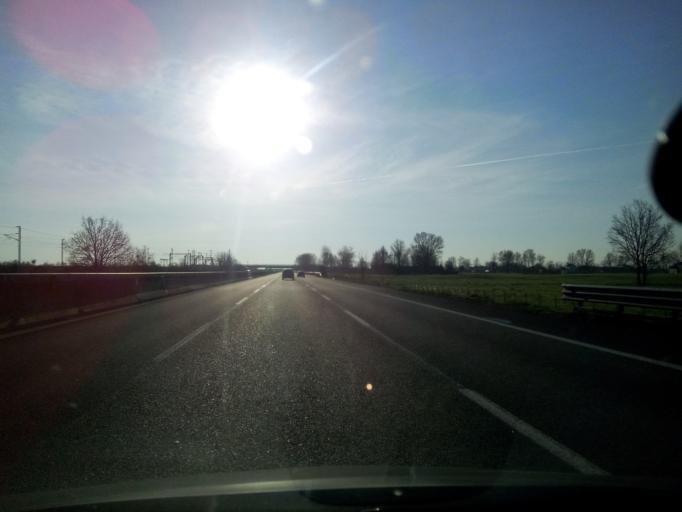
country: IT
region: Emilia-Romagna
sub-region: Provincia di Parma
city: Fontanellato
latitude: 44.8797
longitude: 10.1514
